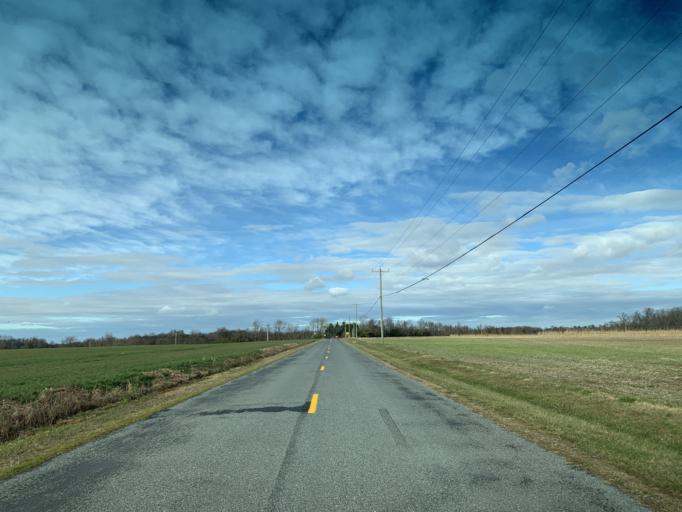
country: US
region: Maryland
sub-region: Kent County
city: Chestertown
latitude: 39.3463
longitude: -76.0536
